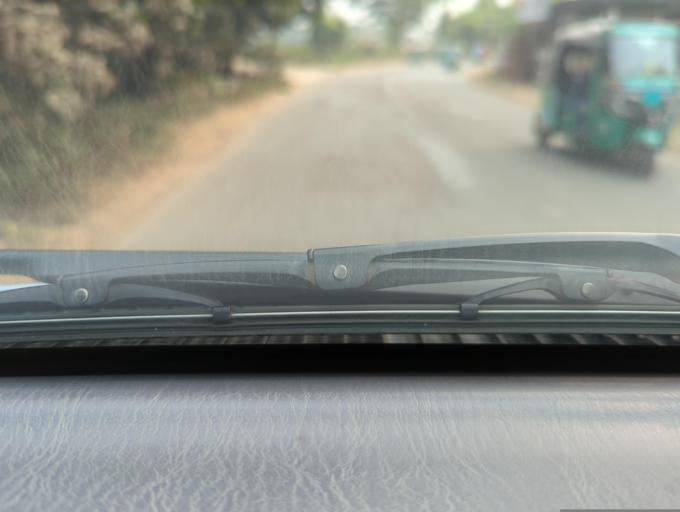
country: BD
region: Sylhet
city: Maulavi Bazar
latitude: 24.4956
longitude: 91.7462
